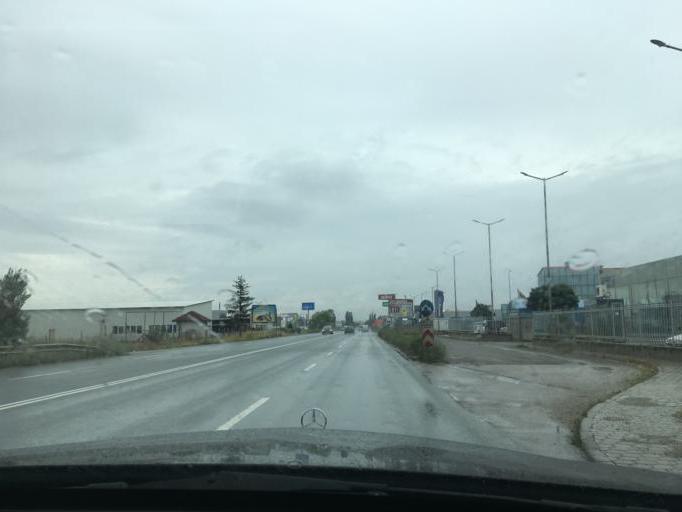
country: BG
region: Sofiya
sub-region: Obshtina Bozhurishte
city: Bozhurishte
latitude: 42.7426
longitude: 23.2336
